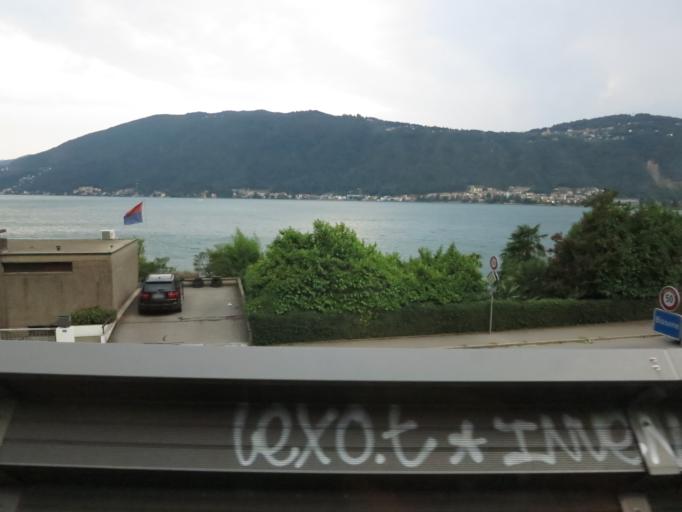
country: CH
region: Ticino
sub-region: Lugano District
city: Melide
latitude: 45.9481
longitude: 8.9666
